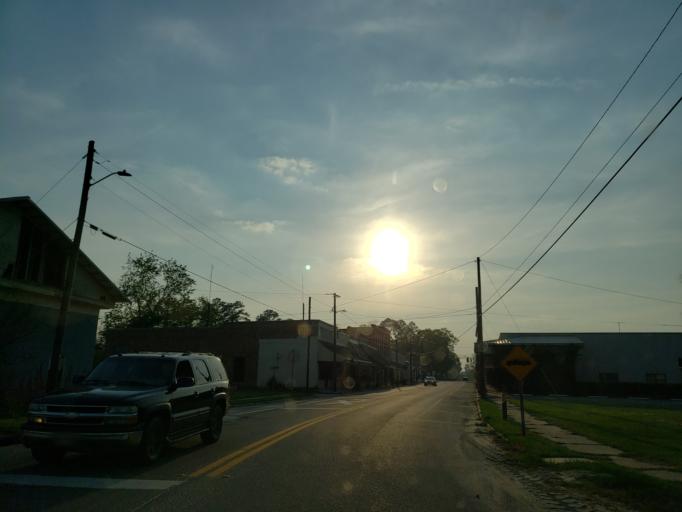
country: US
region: Georgia
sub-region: Cook County
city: Sparks
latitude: 31.1669
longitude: -83.4357
